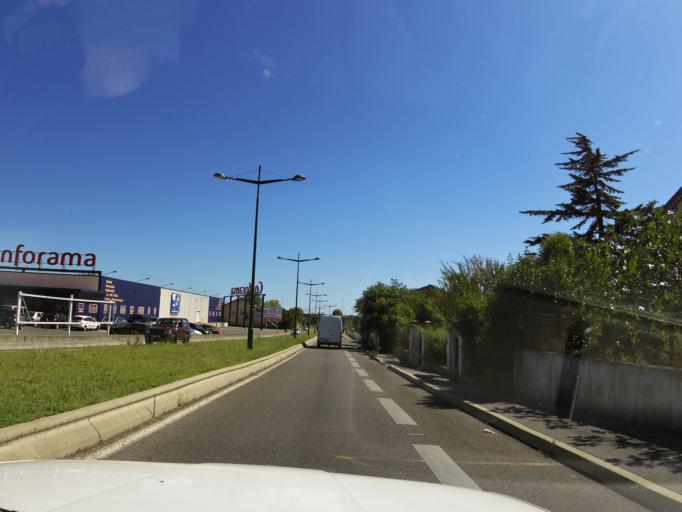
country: FR
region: Languedoc-Roussillon
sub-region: Departement du Gard
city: Ales
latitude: 44.1112
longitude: 4.1001
